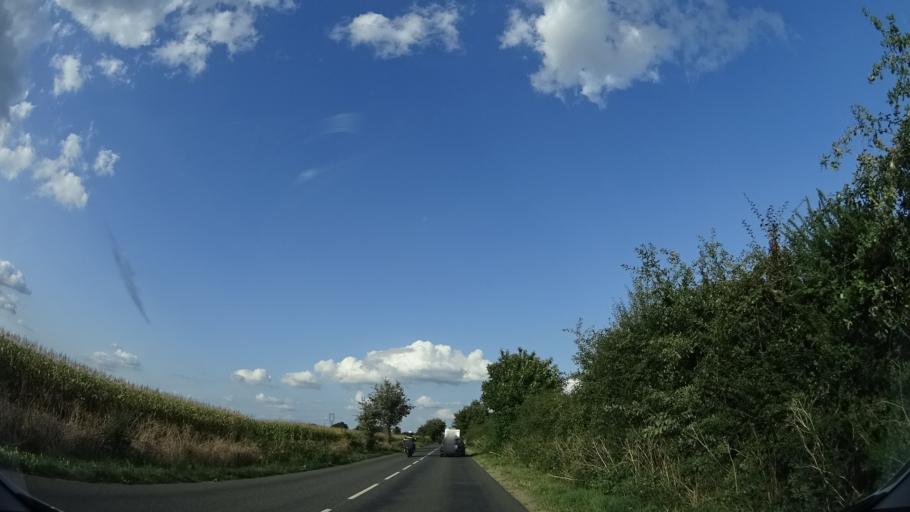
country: FR
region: Pays de la Loire
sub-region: Departement de la Loire-Atlantique
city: Casson
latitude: 47.4140
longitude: -1.5301
